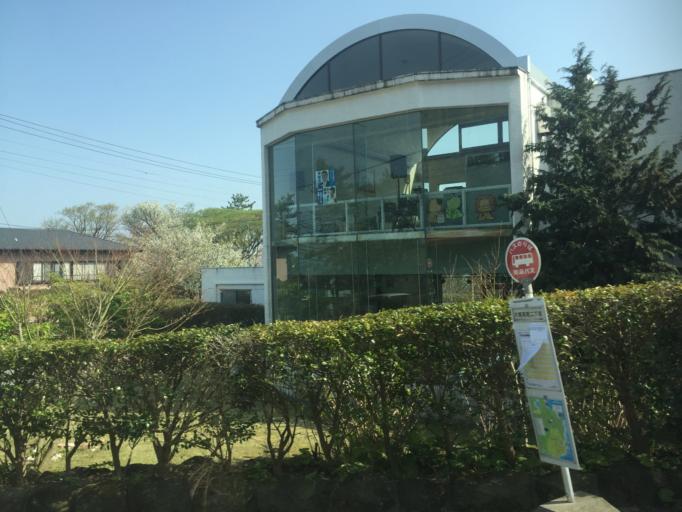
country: JP
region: Shizuoka
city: Ito
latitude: 34.9049
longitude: 139.1039
